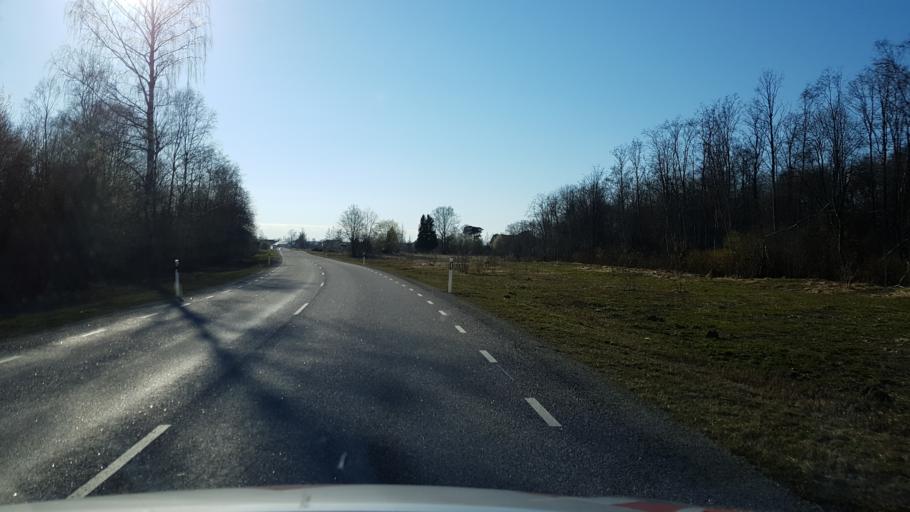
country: EE
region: Ida-Virumaa
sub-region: Kohtla-Jaerve linn
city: Kohtla-Jarve
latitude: 59.3371
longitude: 27.3060
